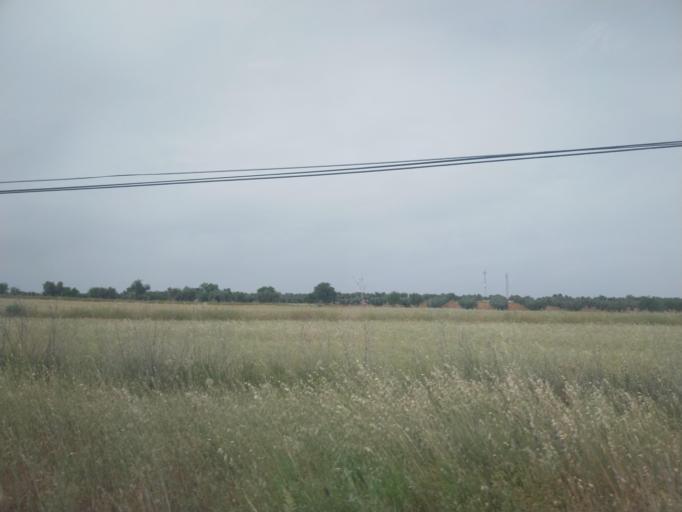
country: ES
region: Castille-La Mancha
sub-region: Province of Toledo
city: Casasbuenas
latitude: 39.7623
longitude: -4.1341
